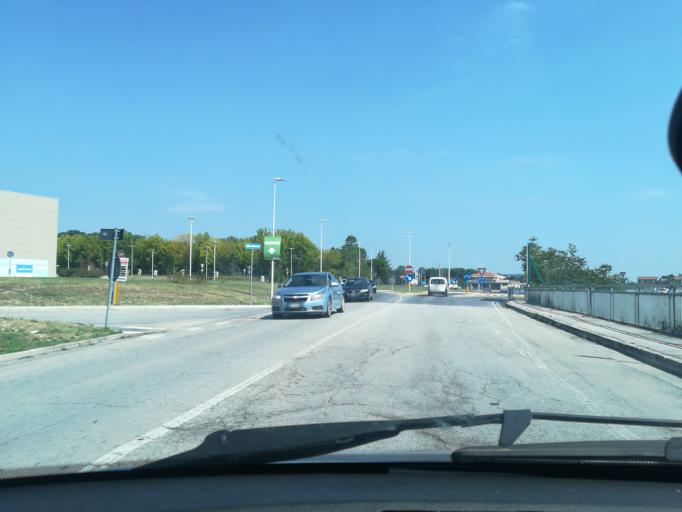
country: IT
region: The Marches
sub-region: Provincia di Macerata
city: Tolentino
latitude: 43.2166
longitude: 13.3105
